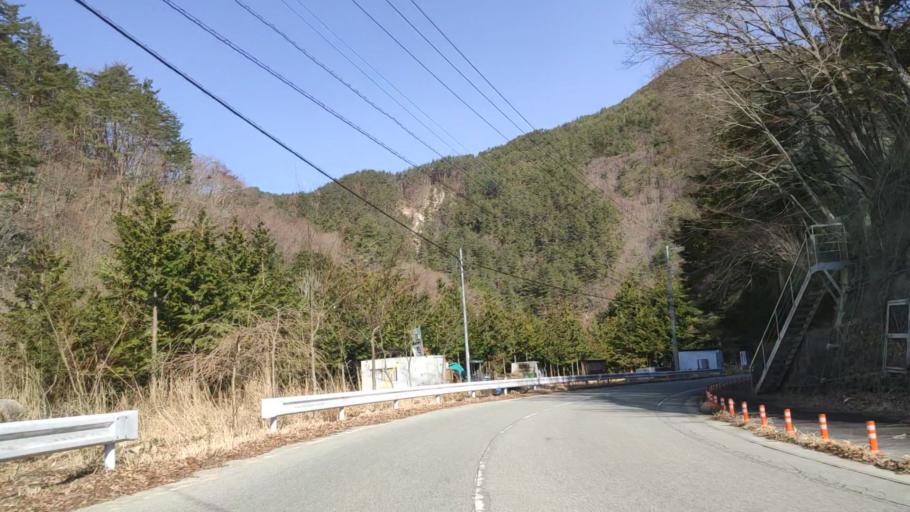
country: JP
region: Yamanashi
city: Fujikawaguchiko
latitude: 35.5493
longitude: 138.6589
